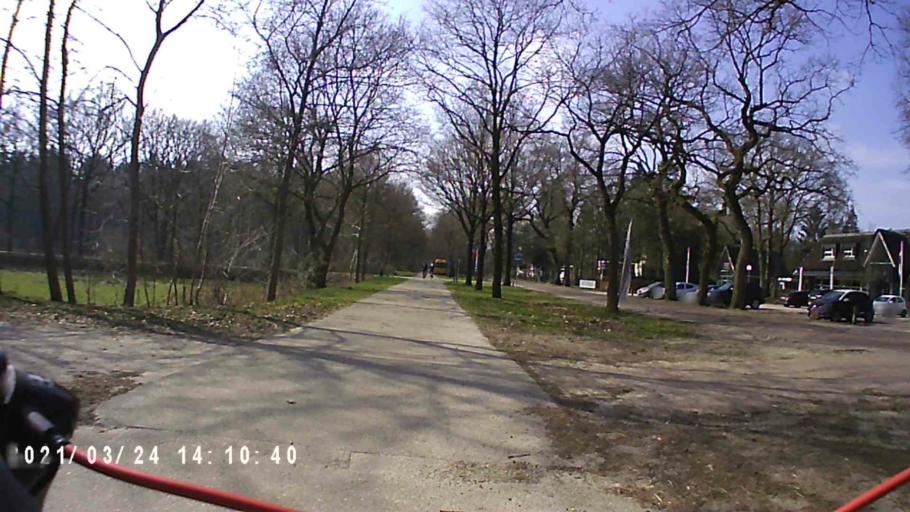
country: NL
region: Friesland
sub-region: Gemeente Smallingerland
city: Drachtstercompagnie
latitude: 53.0695
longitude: 6.2308
